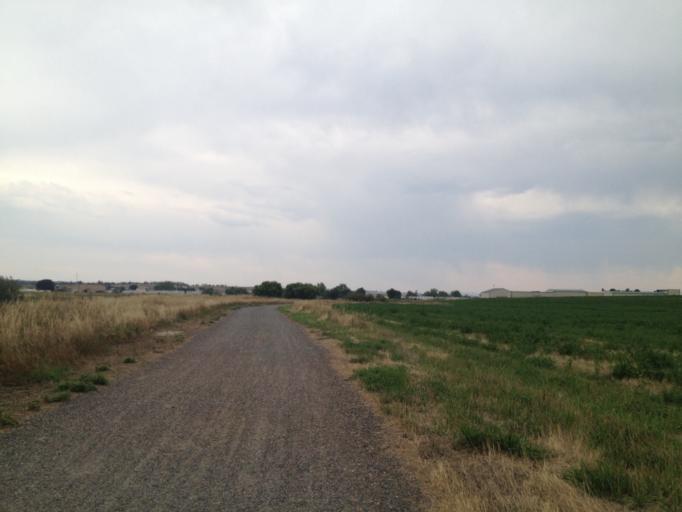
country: US
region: Colorado
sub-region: Boulder County
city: Erie
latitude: 40.0144
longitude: -105.0511
